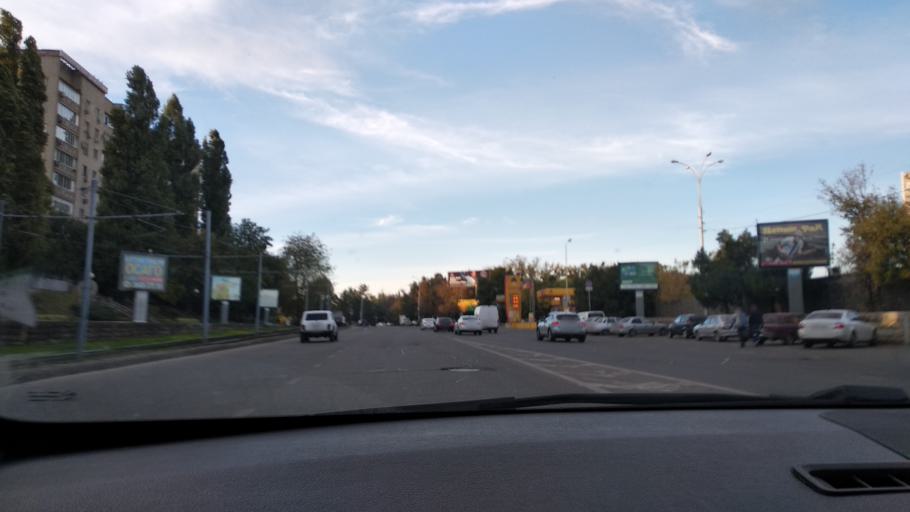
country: RU
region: Krasnodarskiy
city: Krasnodar
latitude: 45.0221
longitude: 38.9974
